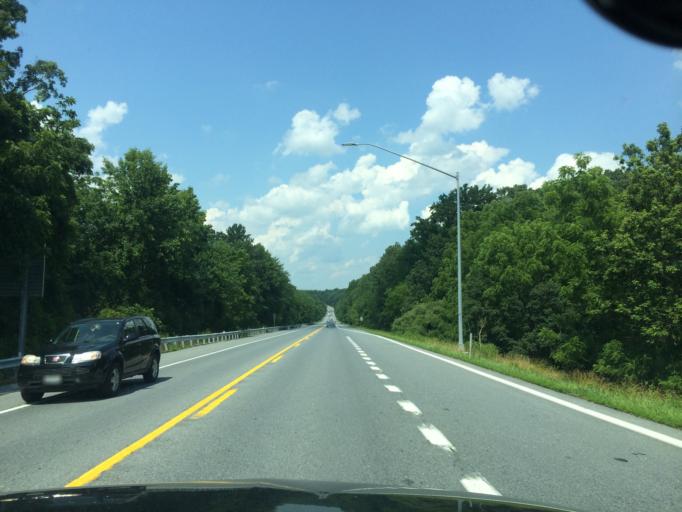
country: US
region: Maryland
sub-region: Carroll County
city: Eldersburg
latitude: 39.4330
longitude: -77.0051
